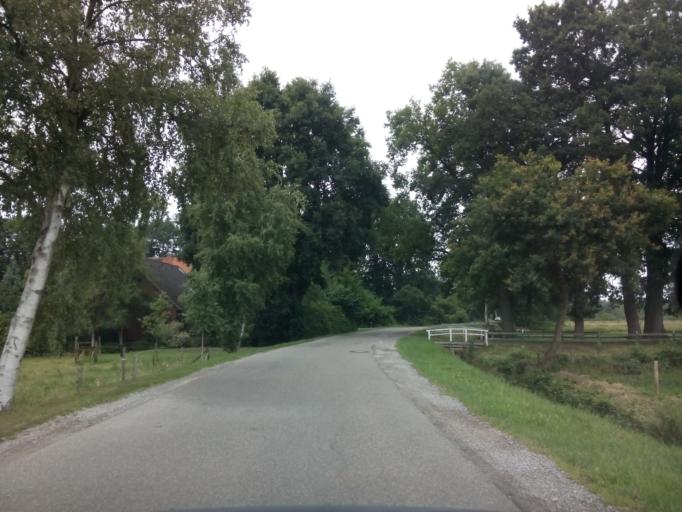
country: DE
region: Lower Saxony
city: Worpswede
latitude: 53.2102
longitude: 8.9024
